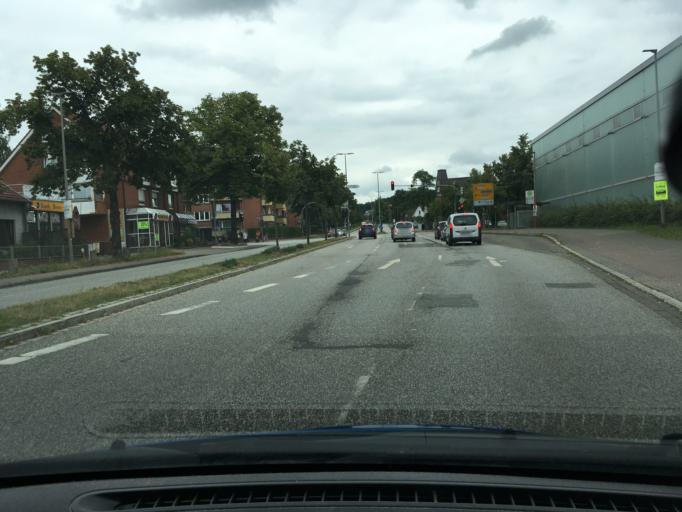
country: DE
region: Schleswig-Holstein
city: Geesthacht
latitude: 53.4367
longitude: 10.3721
